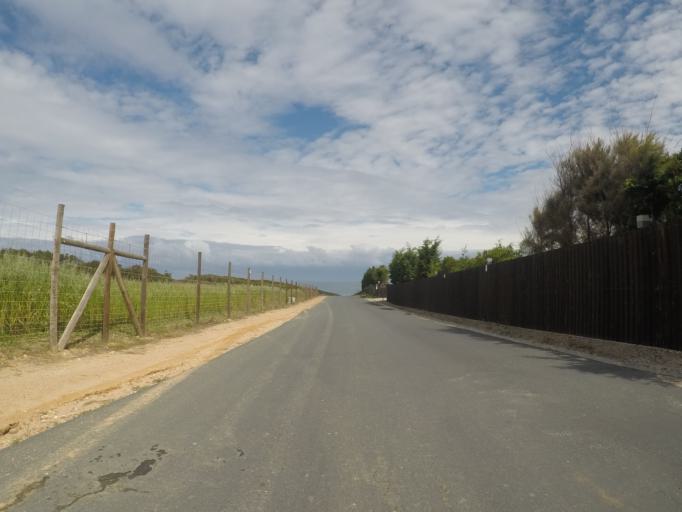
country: PT
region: Beja
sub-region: Odemira
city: Sao Teotonio
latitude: 37.4967
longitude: -8.7898
